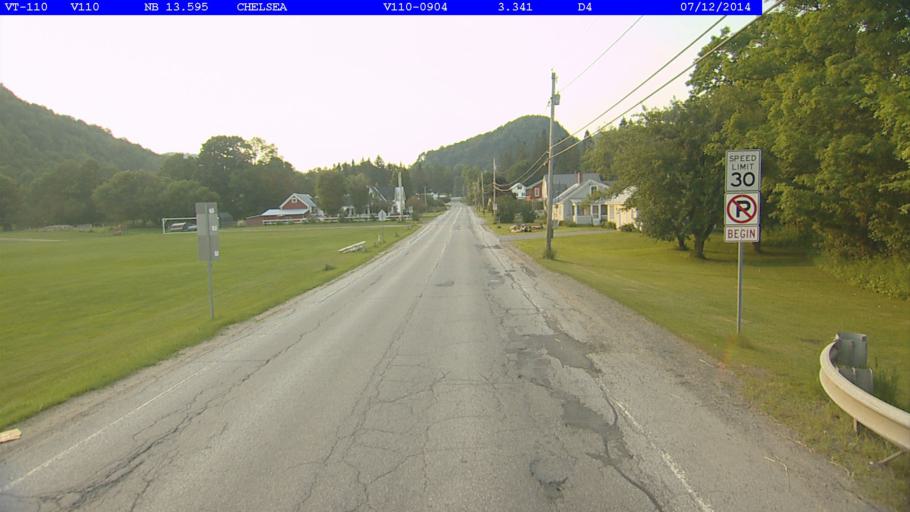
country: US
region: Vermont
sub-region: Orange County
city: Chelsea
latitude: 43.9945
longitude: -72.4472
